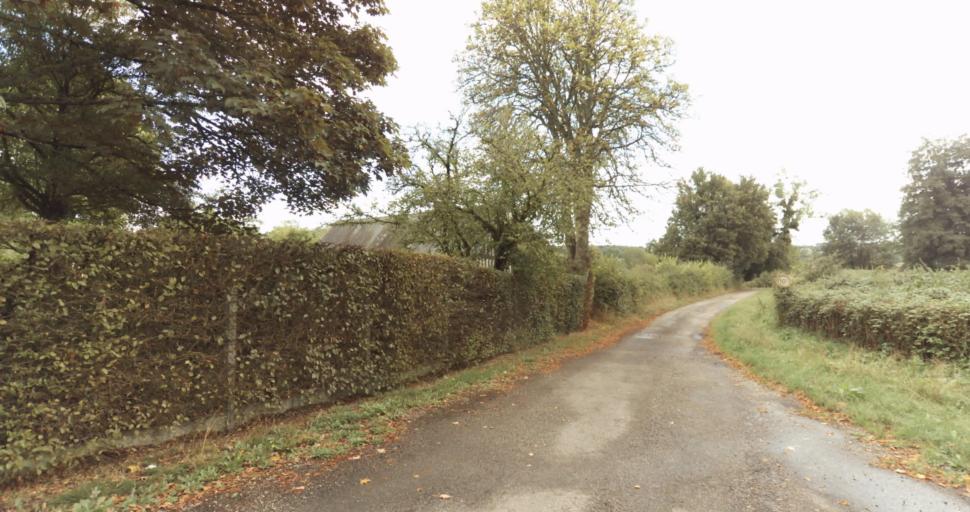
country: FR
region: Lower Normandy
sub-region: Departement de l'Orne
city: Vimoutiers
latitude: 48.8890
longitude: 0.1765
